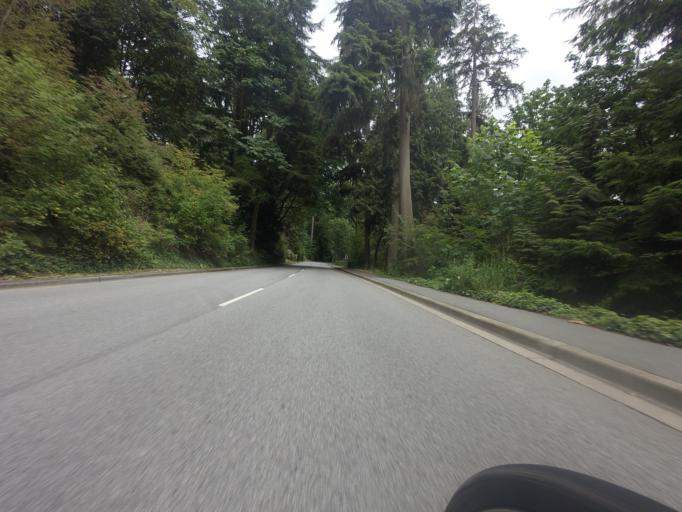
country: CA
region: British Columbia
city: West End
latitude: 49.3041
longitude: -123.1536
